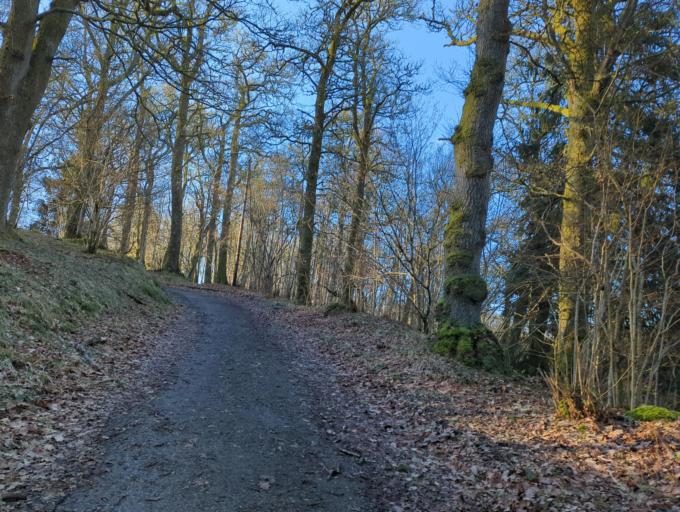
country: GB
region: Scotland
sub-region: Perth and Kinross
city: Bankfoot
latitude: 56.5515
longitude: -3.6341
